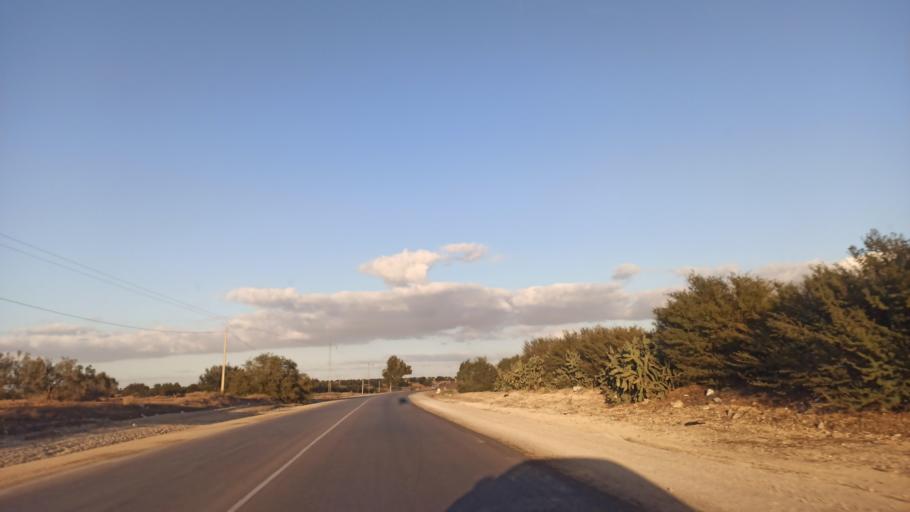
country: TN
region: Al Qayrawan
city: Sbikha
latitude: 35.8752
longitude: 10.2212
